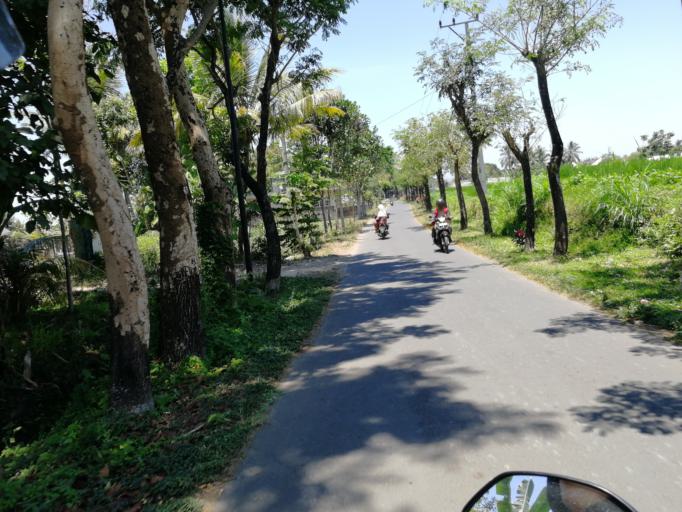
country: ID
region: West Nusa Tenggara
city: Tetebatu
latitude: -8.5584
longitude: 116.4196
